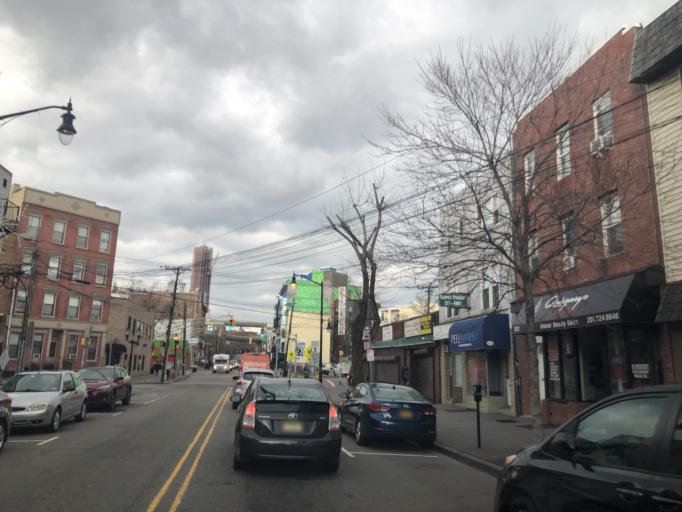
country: US
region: New Jersey
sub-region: Hudson County
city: Hoboken
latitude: 40.7240
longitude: -74.0503
